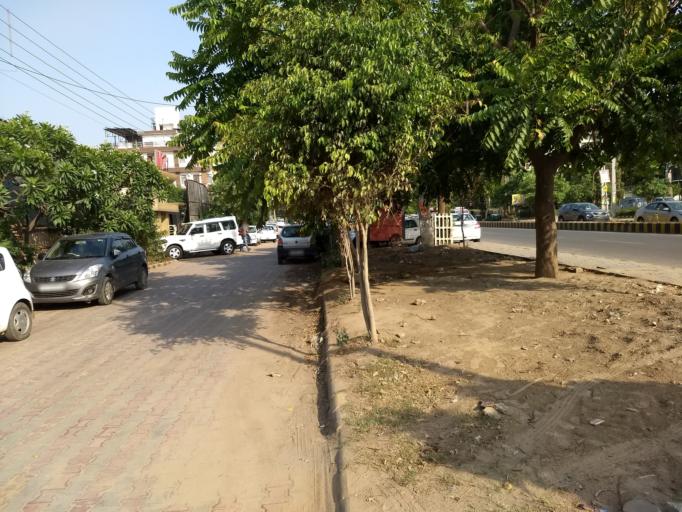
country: IN
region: Haryana
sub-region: Gurgaon
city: Gurgaon
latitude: 28.4333
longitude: 77.0720
